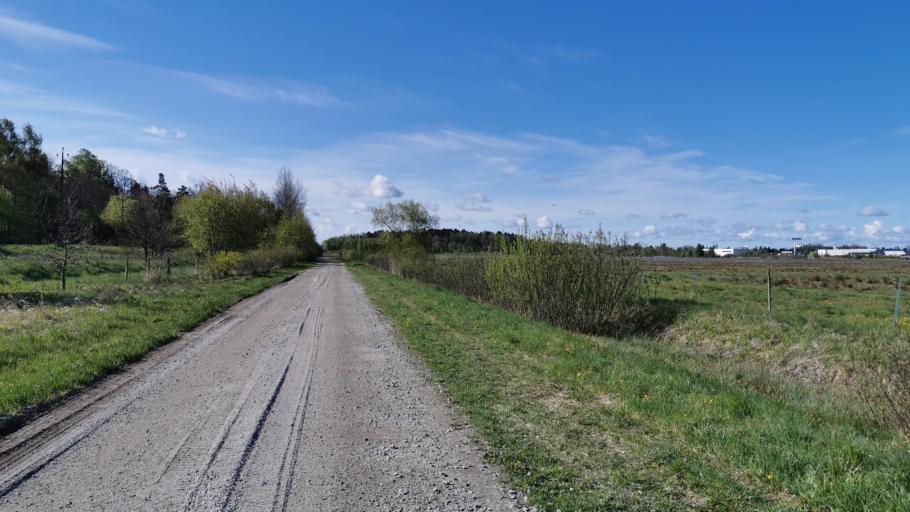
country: SE
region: OErebro
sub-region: Orebro Kommun
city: Orebro
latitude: 59.3049
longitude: 15.2206
